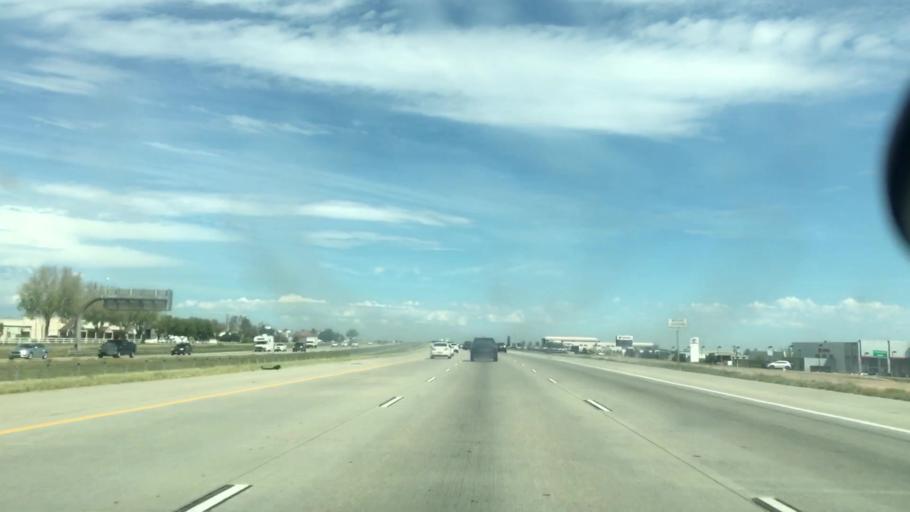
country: US
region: Colorado
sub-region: Weld County
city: Firestone
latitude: 40.1158
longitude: -104.9794
